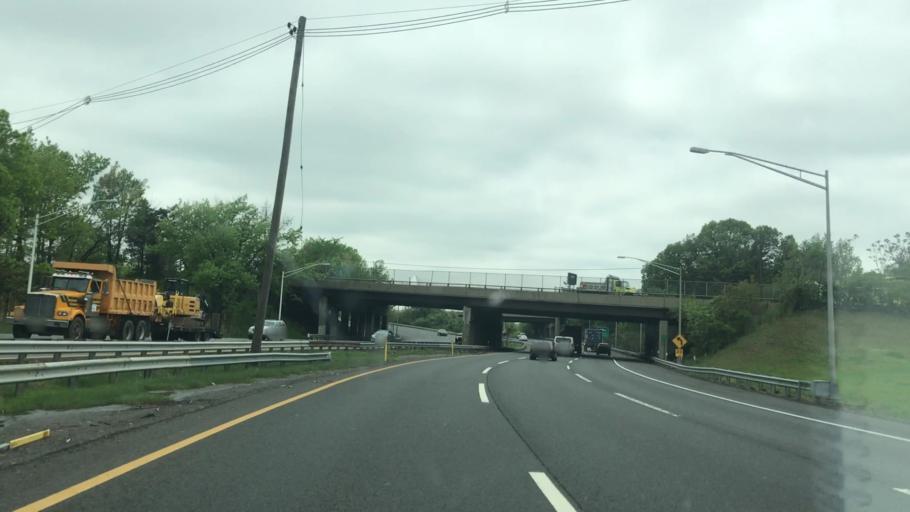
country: US
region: New Jersey
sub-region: Middlesex County
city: Woodbridge
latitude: 40.5415
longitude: -74.2912
